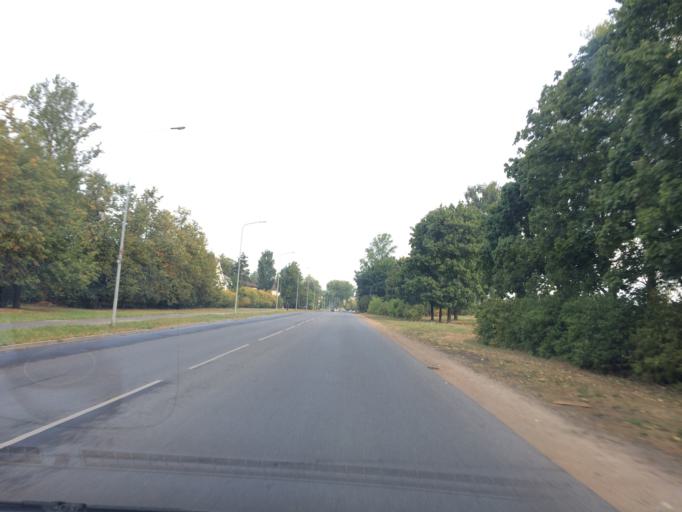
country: LV
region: Kekava
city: Balozi
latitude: 56.9109
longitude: 24.1979
